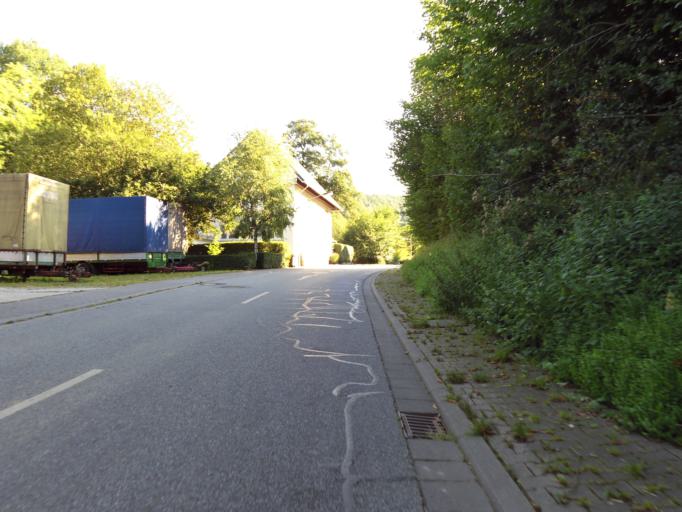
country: DE
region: Hesse
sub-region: Regierungsbezirk Darmstadt
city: Heppenheim an der Bergstrasse
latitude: 49.6652
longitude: 8.6601
